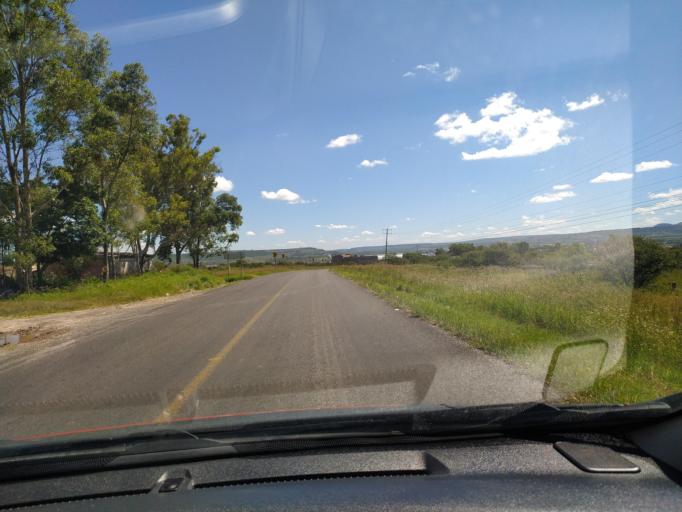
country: MX
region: Jalisco
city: San Miguel el Alto
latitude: 21.0247
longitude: -102.4308
